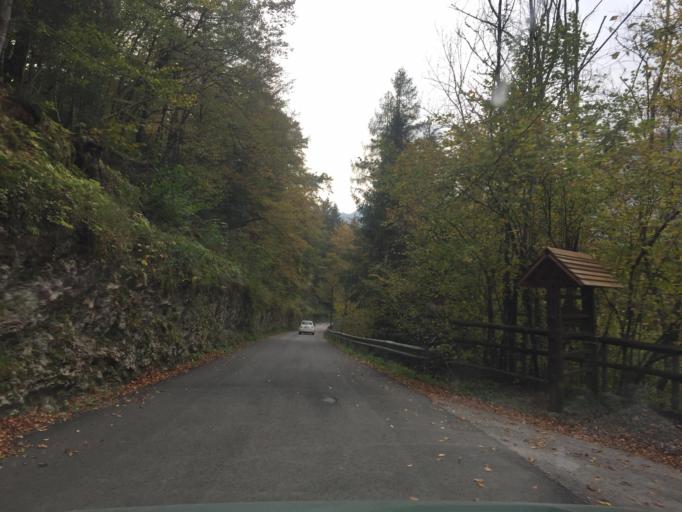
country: IT
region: Friuli Venezia Giulia
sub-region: Provincia di Pordenone
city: Andreis
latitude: 46.1994
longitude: 12.6293
